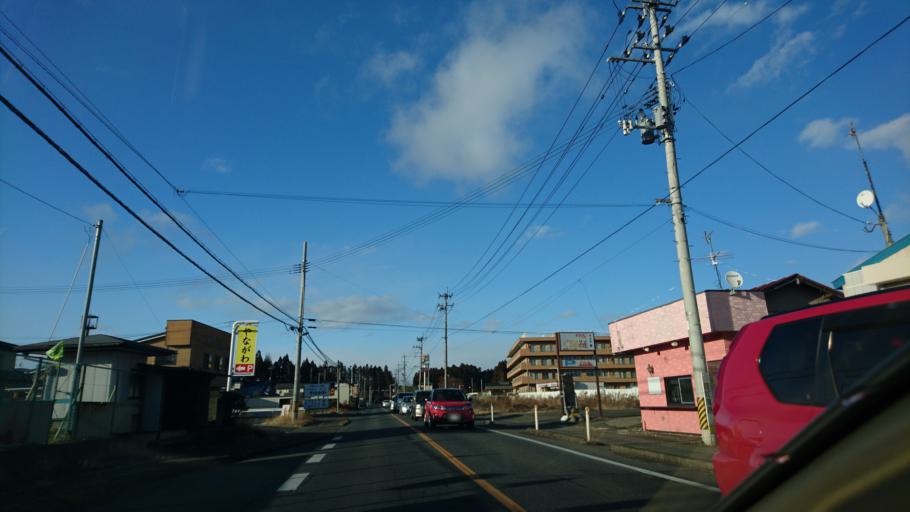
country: JP
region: Miyagi
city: Tomiya
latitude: 38.4649
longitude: 140.8700
